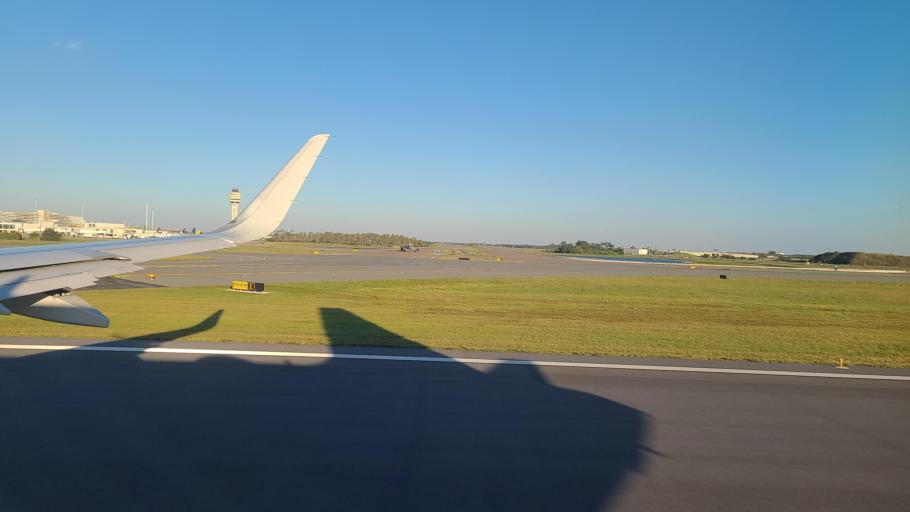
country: US
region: Florida
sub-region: Orange County
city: Taft
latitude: 28.4226
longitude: -81.3219
